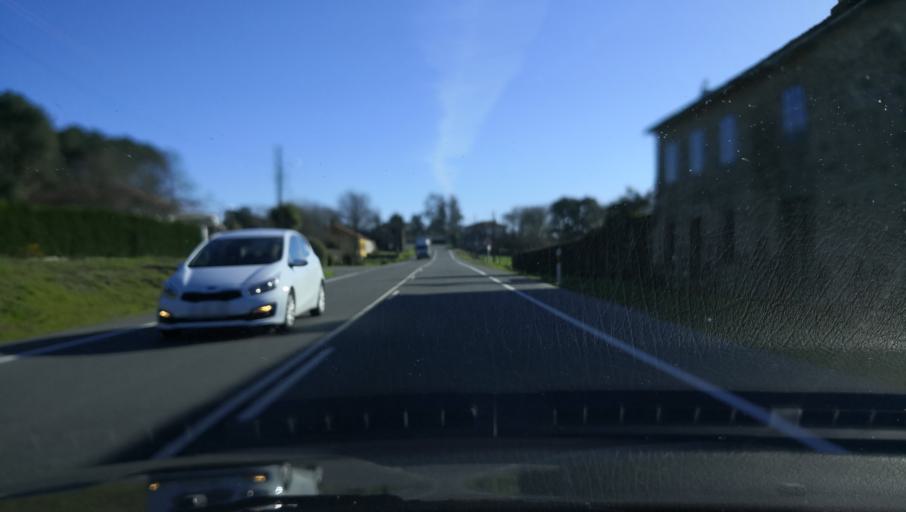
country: ES
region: Galicia
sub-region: Provincia da Coruna
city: Ribeira
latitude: 42.7545
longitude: -8.3737
